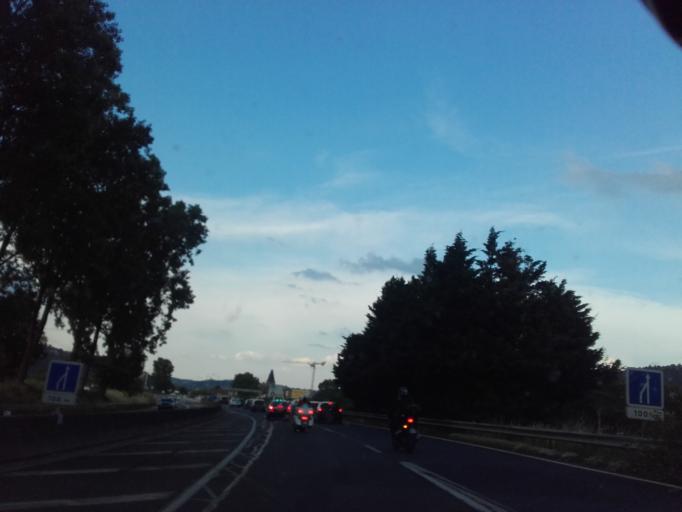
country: FR
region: Rhone-Alpes
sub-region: Departement du Rhone
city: Saint-Cyr-sur-le-Rhone
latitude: 45.5003
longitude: 4.8447
